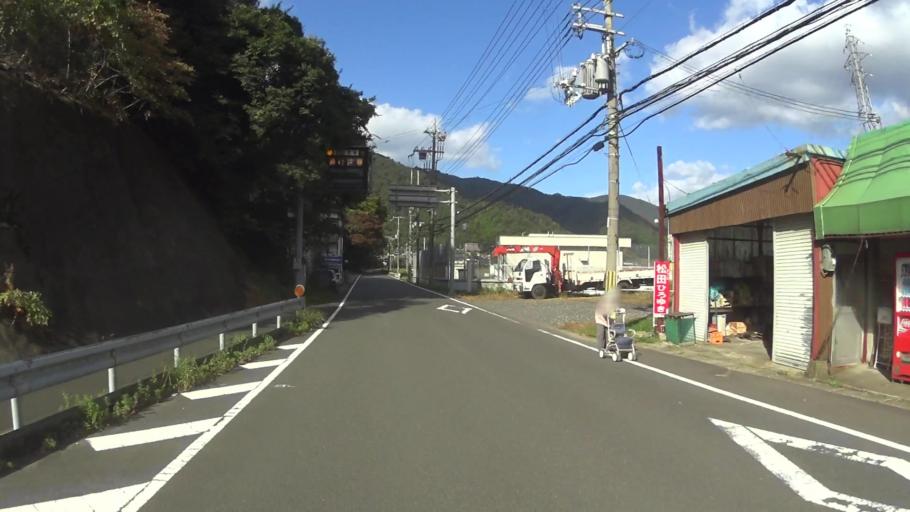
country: JP
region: Kyoto
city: Maizuru
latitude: 35.5165
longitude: 135.4024
